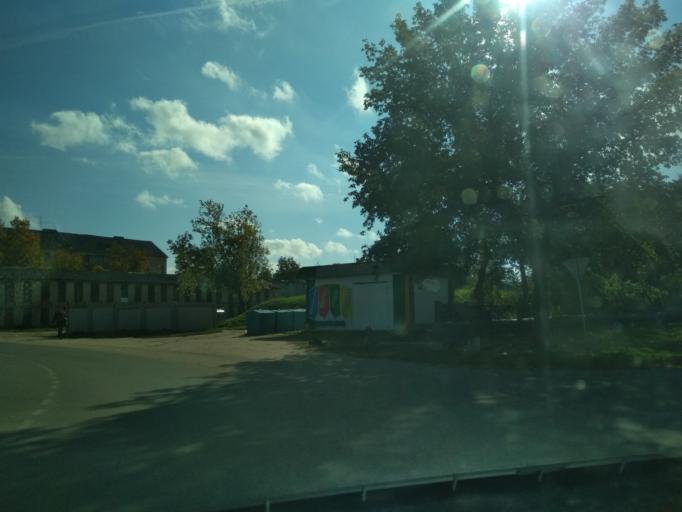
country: BY
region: Minsk
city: Mar''ina Horka
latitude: 53.5022
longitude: 28.1664
